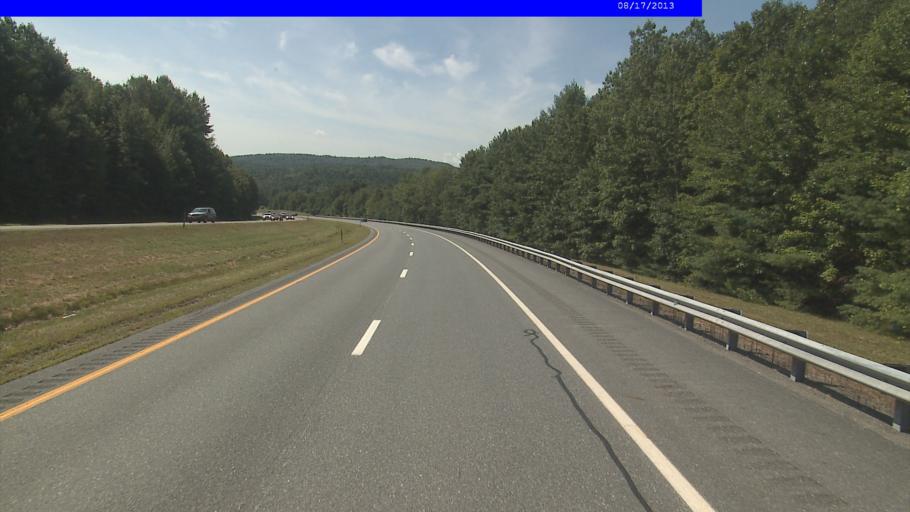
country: US
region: Vermont
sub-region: Windham County
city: Brattleboro
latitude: 42.8221
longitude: -72.5695
